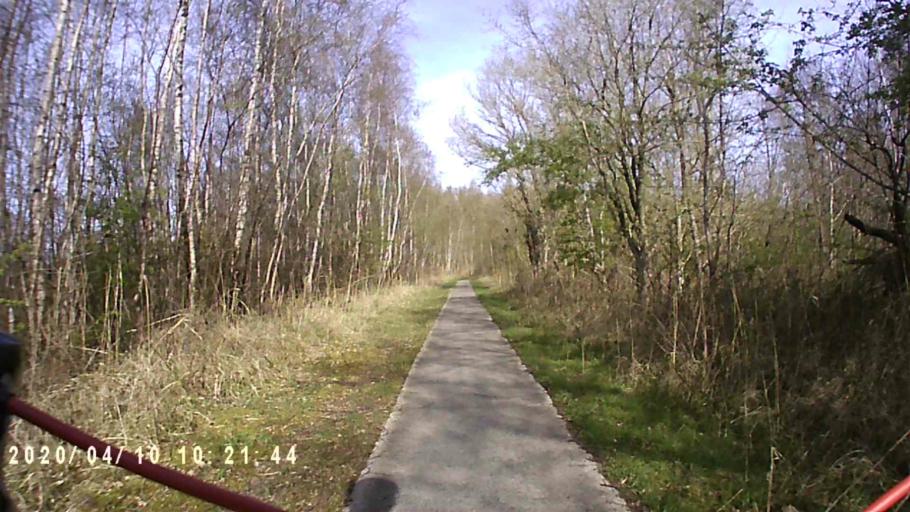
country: NL
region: Friesland
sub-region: Gemeente Dongeradeel
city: Anjum
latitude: 53.3814
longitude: 6.2163
